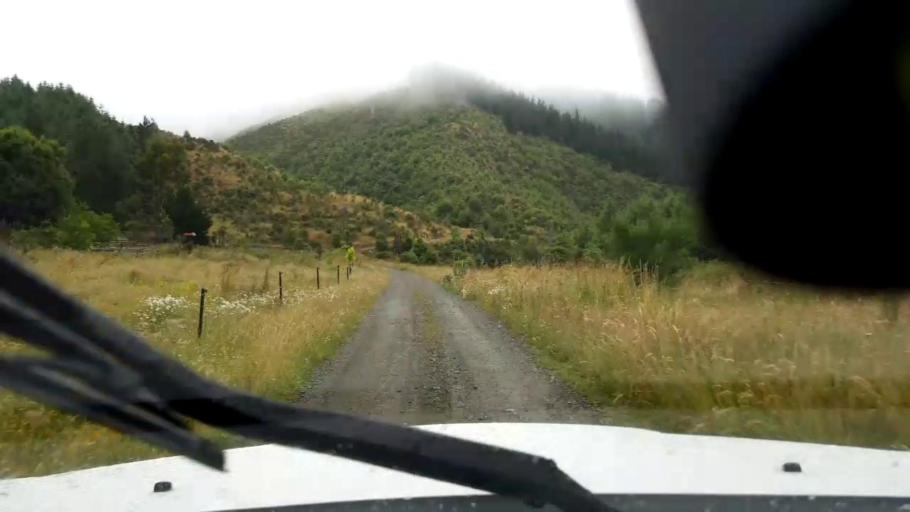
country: NZ
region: Canterbury
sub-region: Timaru District
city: Pleasant Point
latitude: -44.0459
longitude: 171.0220
